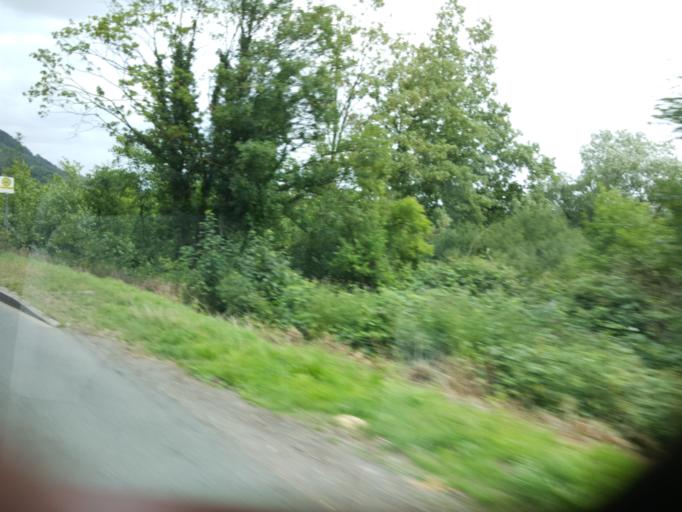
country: DE
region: North Rhine-Westphalia
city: Porta Westfalica
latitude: 52.2447
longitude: 8.8605
